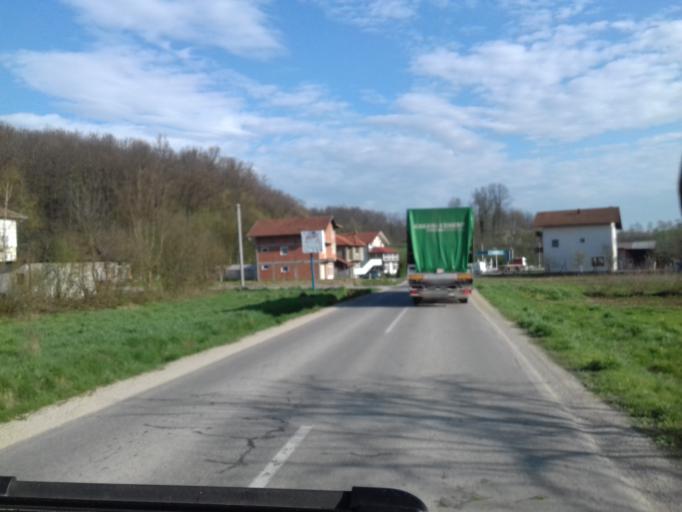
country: BA
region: Federation of Bosnia and Herzegovina
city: Tesanjka
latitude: 44.6559
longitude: 18.0164
